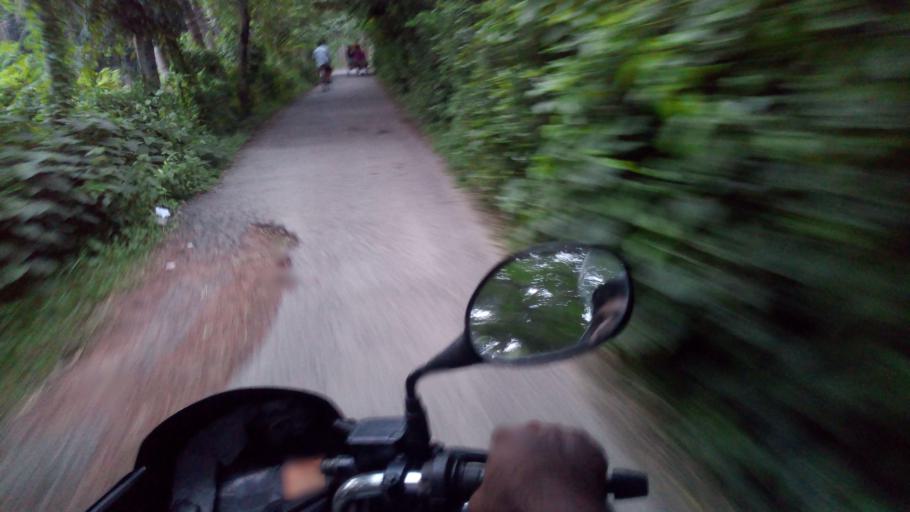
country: BD
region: Khulna
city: Phultala
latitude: 22.7554
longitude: 89.4080
